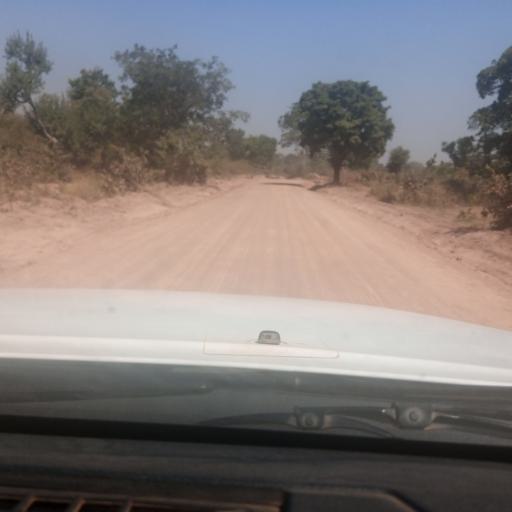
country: NG
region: Adamawa
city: Yola
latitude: 9.0975
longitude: 12.3899
